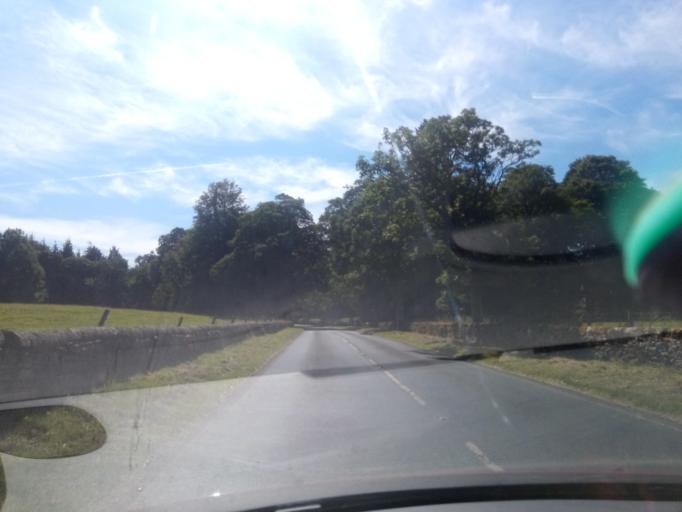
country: GB
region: England
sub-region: Northumberland
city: Bardon Mill
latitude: 54.9031
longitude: -2.3505
